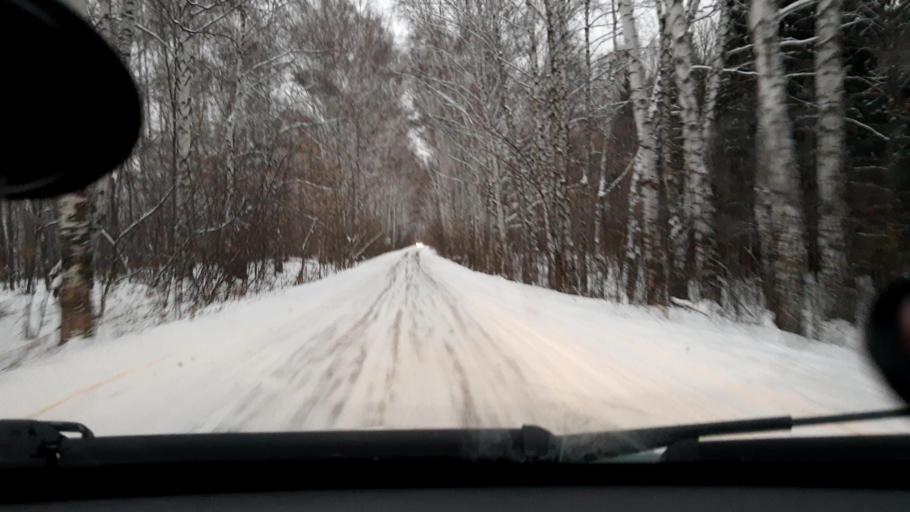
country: RU
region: Bashkortostan
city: Iglino
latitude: 54.8259
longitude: 56.1934
